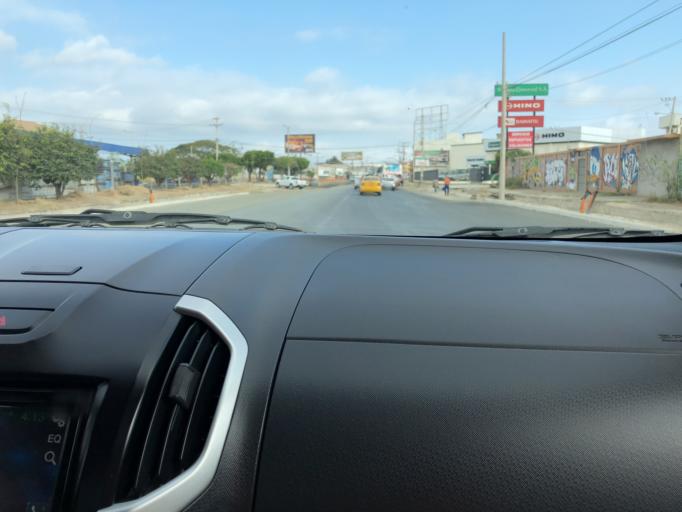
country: EC
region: Manabi
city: Manta
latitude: -0.9750
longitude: -80.6997
